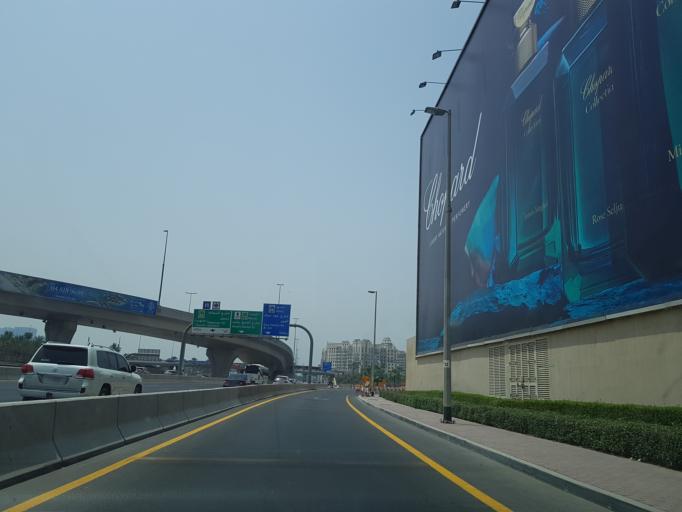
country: AE
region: Ash Shariqah
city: Sharjah
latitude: 25.2281
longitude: 55.3186
